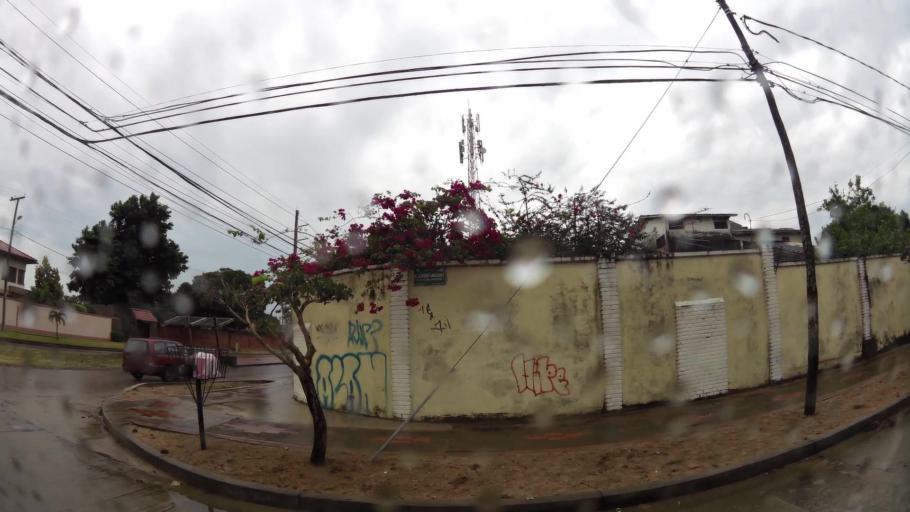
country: BO
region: Santa Cruz
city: Santa Cruz de la Sierra
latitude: -17.8028
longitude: -63.1580
